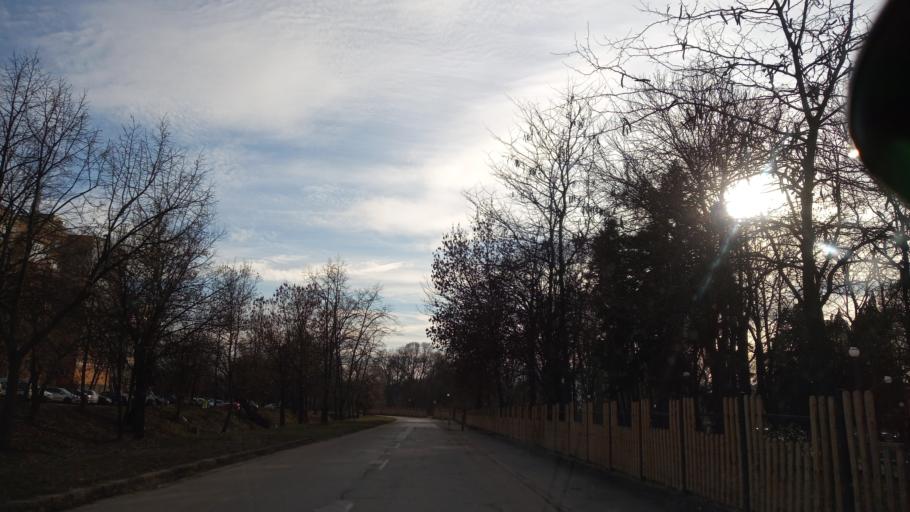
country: BG
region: Sofia-Capital
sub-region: Stolichna Obshtina
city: Bukhovo
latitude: 42.7608
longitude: 23.5621
